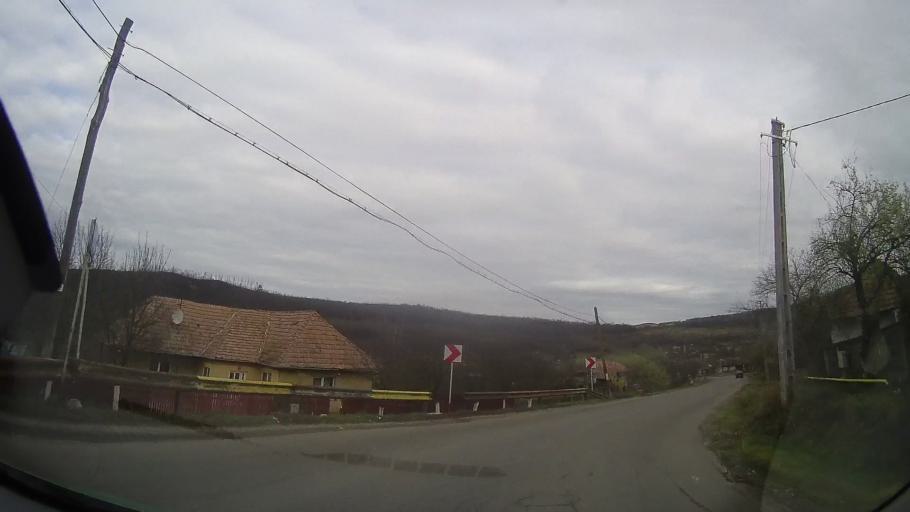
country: RO
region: Bistrita-Nasaud
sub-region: Comuna Silvasu de Campie
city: Silvasu de Campie
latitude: 46.7809
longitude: 24.2920
